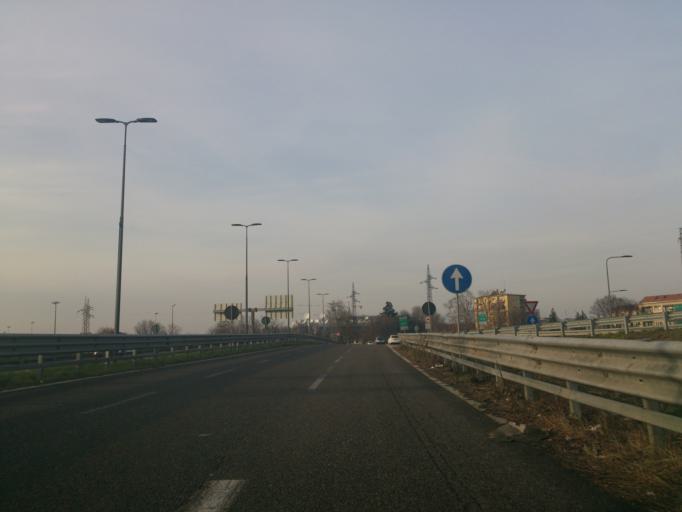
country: IT
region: Lombardy
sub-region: Citta metropolitana di Milano
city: Chiaravalle
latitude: 45.4281
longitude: 9.2449
